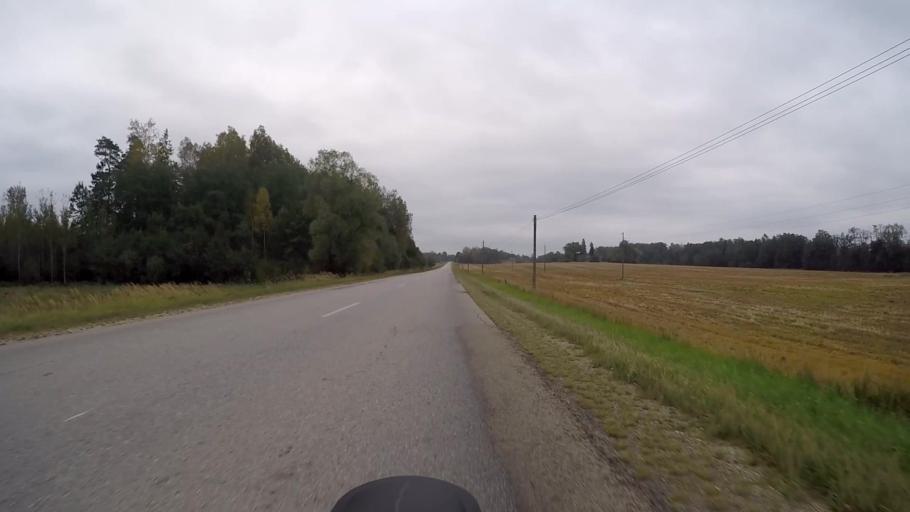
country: LV
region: Seja
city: Loja
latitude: 57.2747
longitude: 24.5649
